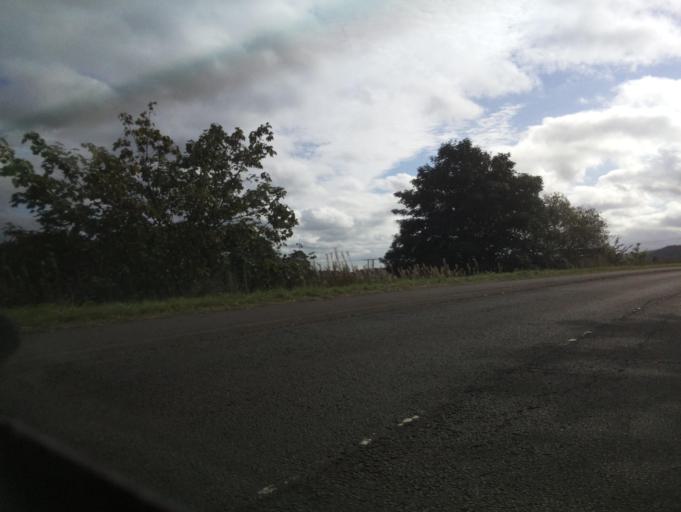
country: GB
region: Scotland
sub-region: Dumfries and Galloway
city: Moffat
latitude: 55.3194
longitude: -3.4456
